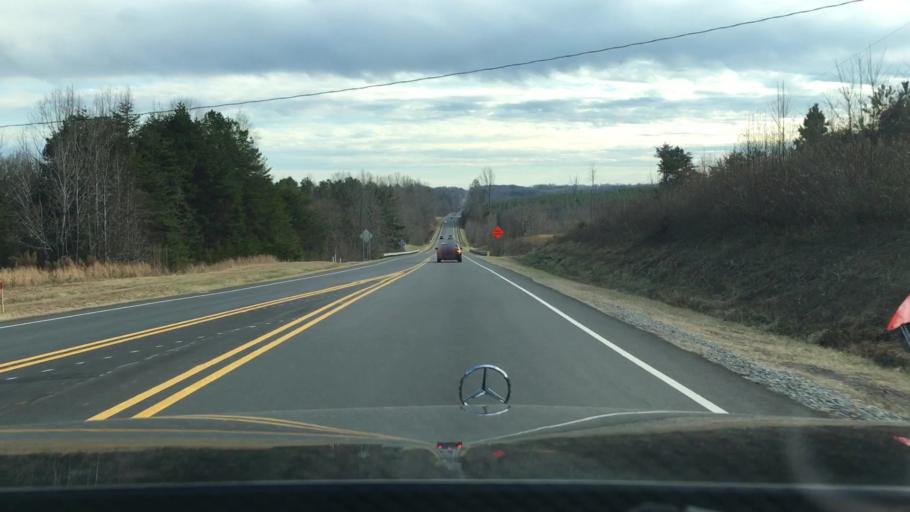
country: US
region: Virginia
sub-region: City of Danville
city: Danville
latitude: 36.5211
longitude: -79.3952
